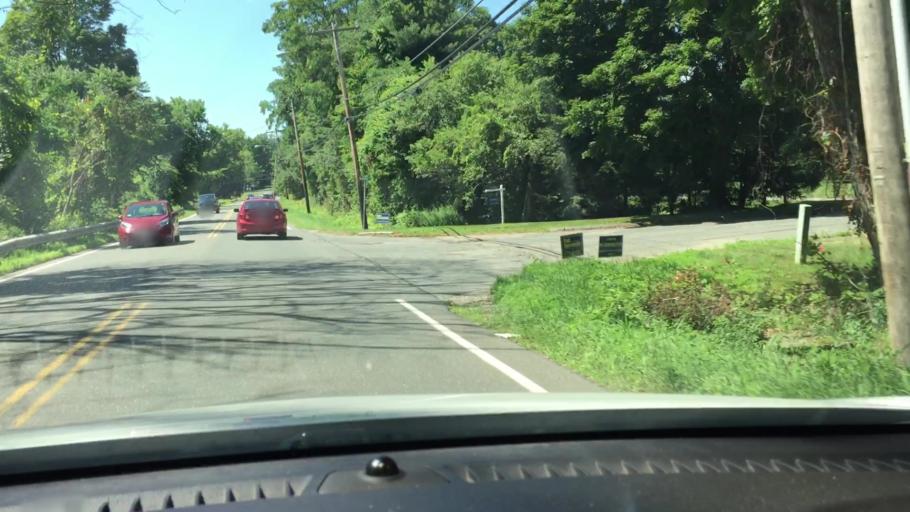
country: US
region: Massachusetts
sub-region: Berkshire County
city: Pittsfield
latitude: 42.4139
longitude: -73.2492
